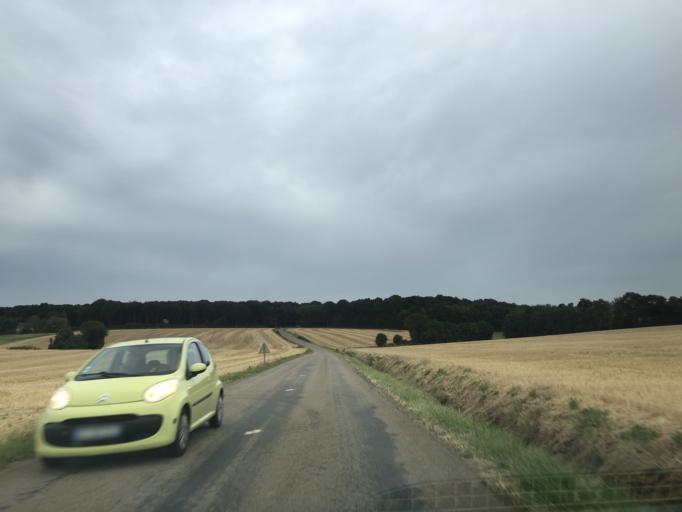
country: FR
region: Bourgogne
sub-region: Departement de l'Yonne
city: Charny
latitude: 47.9665
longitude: 3.1444
